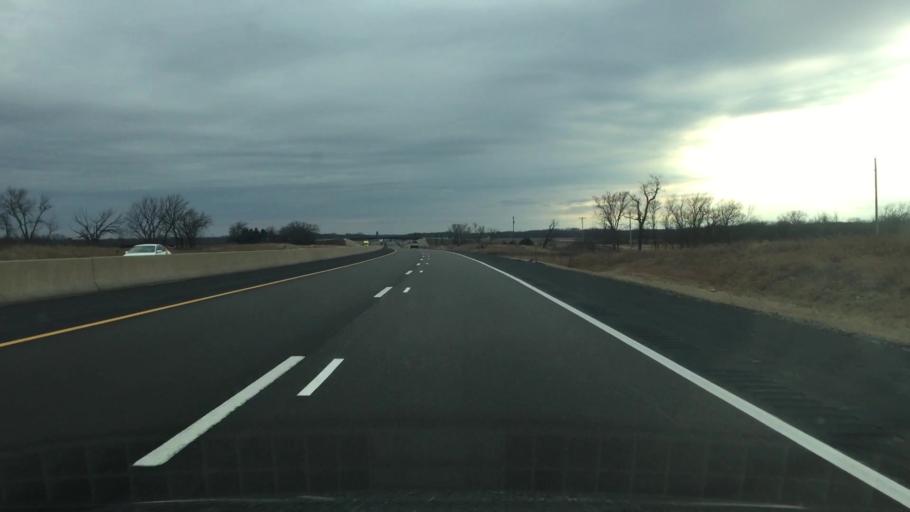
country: US
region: Kansas
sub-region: Lyon County
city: Emporia
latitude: 38.5414
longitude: -96.1313
